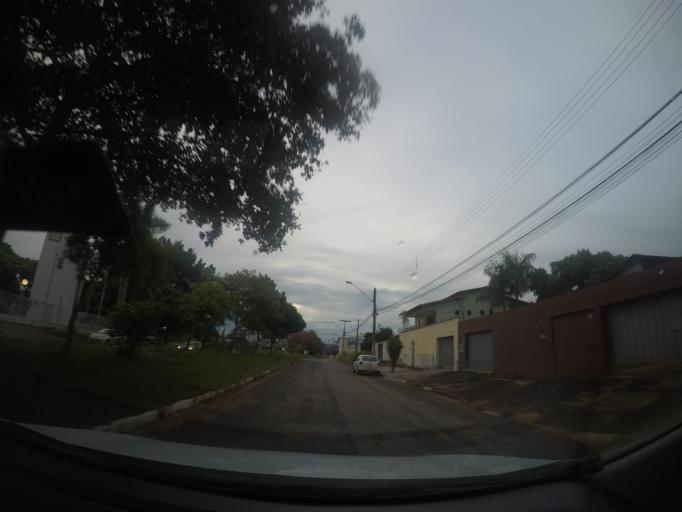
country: BR
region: Goias
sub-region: Goiania
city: Goiania
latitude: -16.6393
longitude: -49.2425
